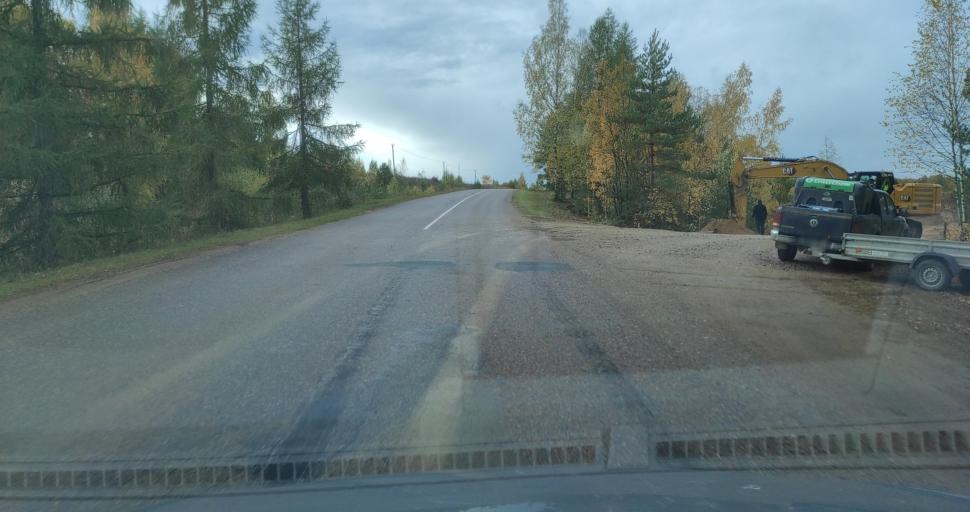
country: LV
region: Skrunda
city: Skrunda
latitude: 56.5893
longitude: 21.9002
